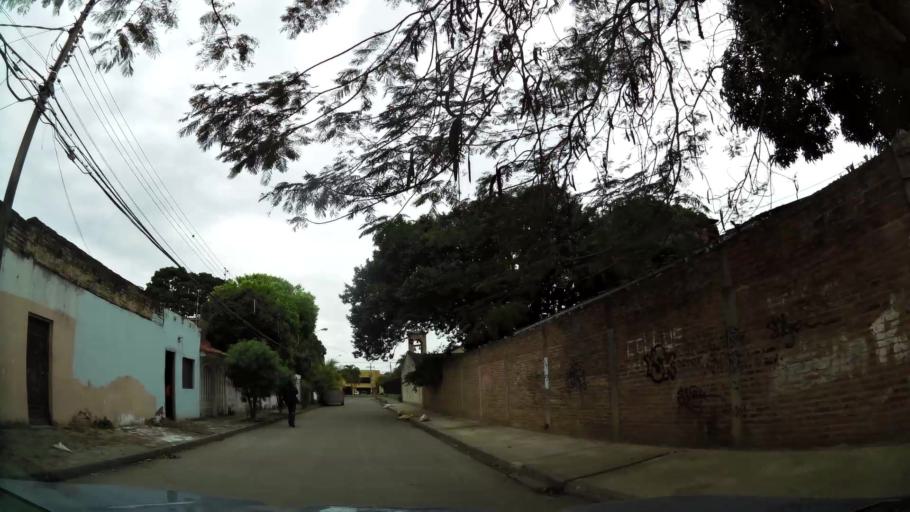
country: BO
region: Santa Cruz
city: Santa Cruz de la Sierra
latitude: -17.7811
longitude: -63.1625
